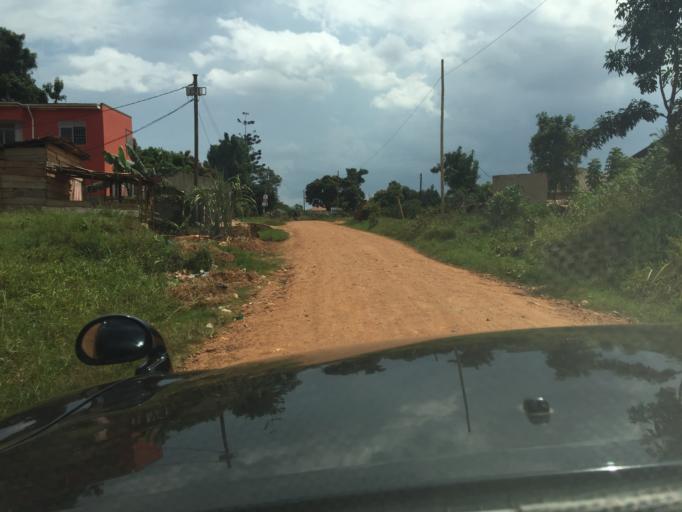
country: UG
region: Central Region
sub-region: Wakiso District
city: Kireka
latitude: 0.4128
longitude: 32.6210
